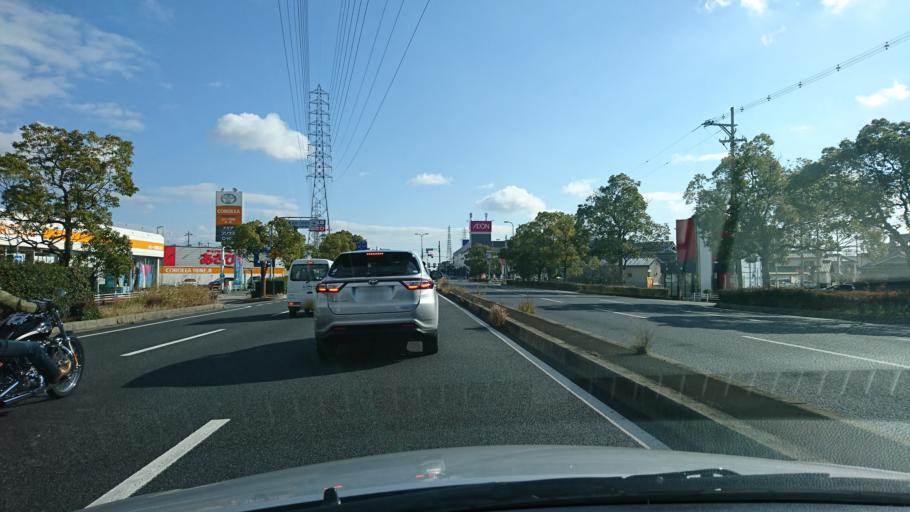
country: JP
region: Hyogo
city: Kakogawacho-honmachi
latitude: 34.7717
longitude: 134.8004
